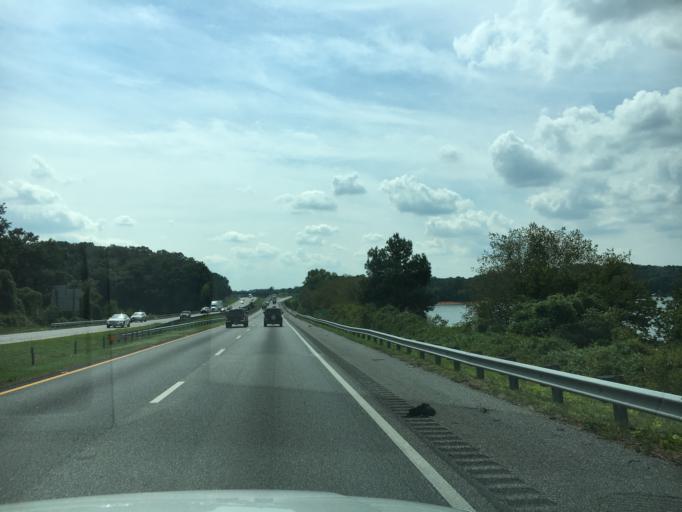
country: US
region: Georgia
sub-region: Franklin County
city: Gumlog
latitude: 34.4938
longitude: -83.0133
